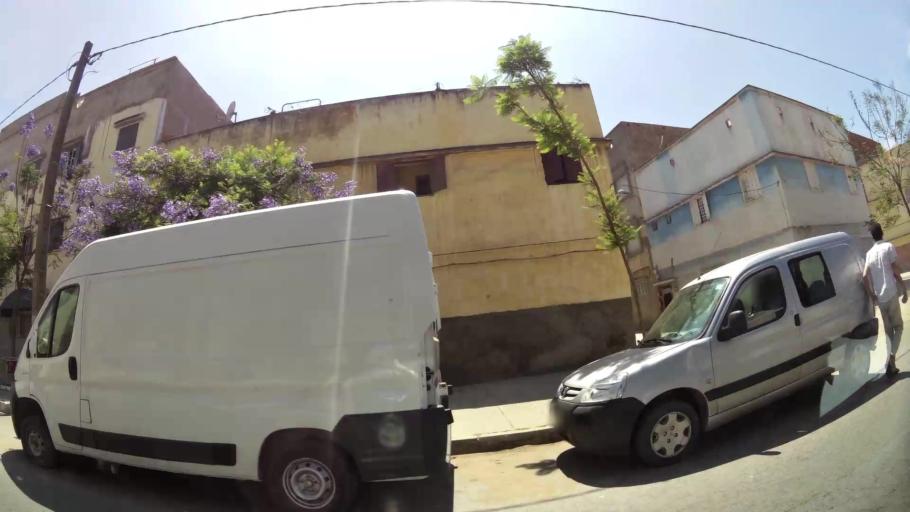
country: MA
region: Gharb-Chrarda-Beni Hssen
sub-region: Kenitra Province
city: Kenitra
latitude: 34.2495
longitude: -6.5454
